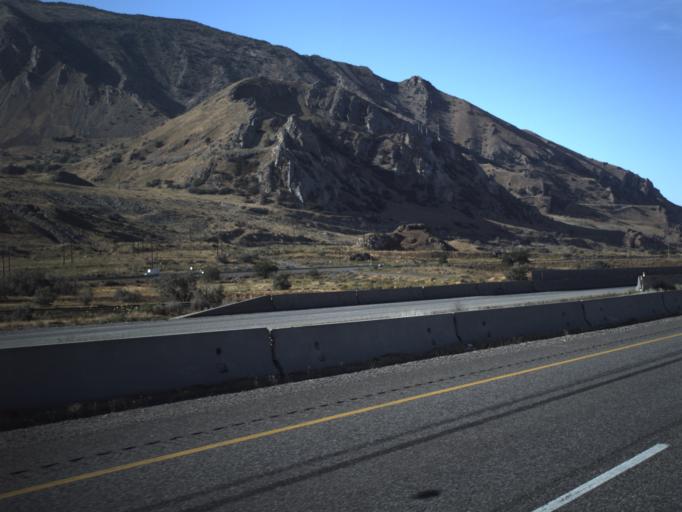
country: US
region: Utah
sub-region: Tooele County
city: Stansbury park
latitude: 40.7260
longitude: -112.2191
